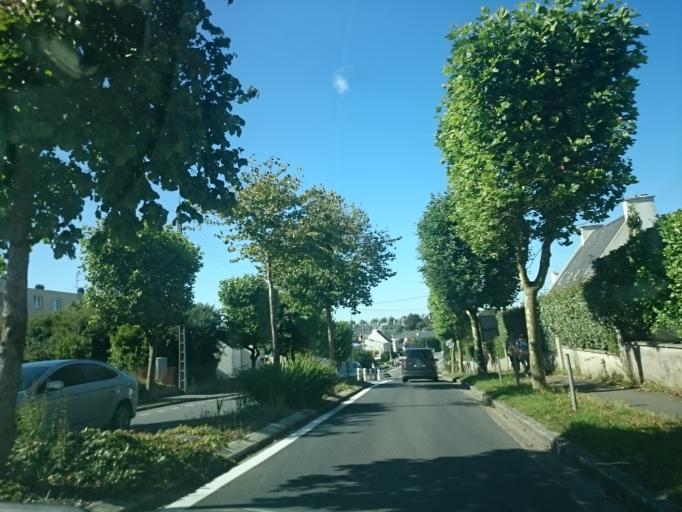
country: FR
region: Brittany
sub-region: Departement du Finistere
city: Brest
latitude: 48.4178
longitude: -4.4870
